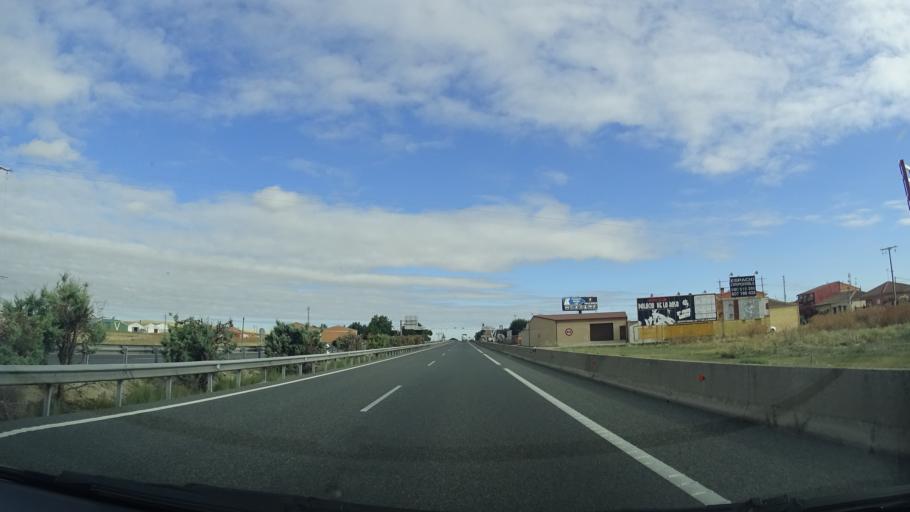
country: ES
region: Castille and Leon
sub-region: Provincia de Valladolid
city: Ataquines
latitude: 41.1787
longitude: -4.8062
